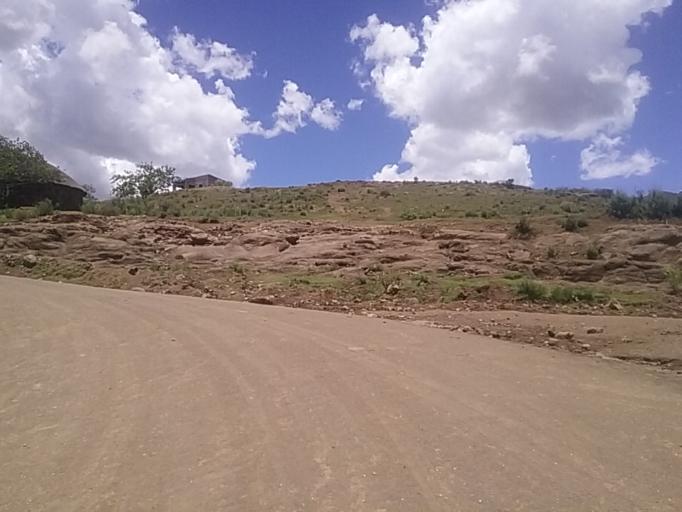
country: LS
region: Qacha's Nek
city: Qacha's Nek
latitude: -30.1692
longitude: 28.2078
